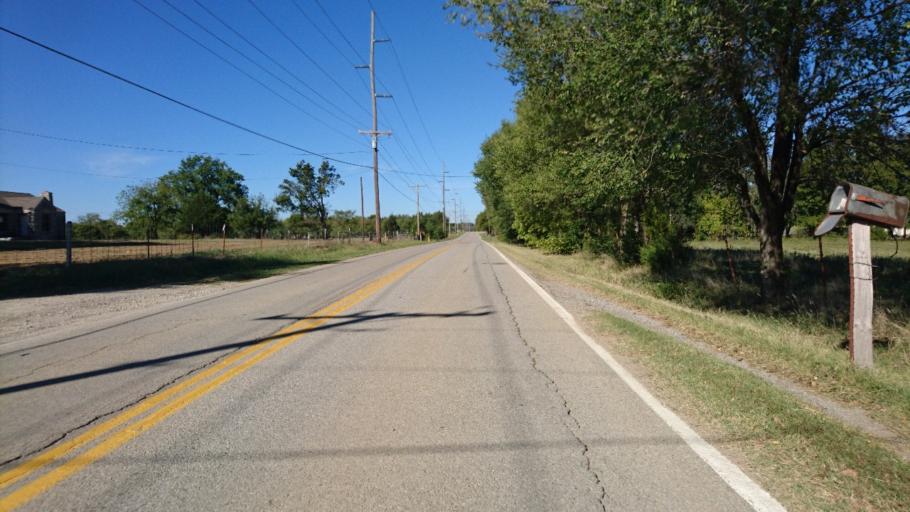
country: US
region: Oklahoma
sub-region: Rogers County
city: Catoosa
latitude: 36.1480
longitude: -95.7730
